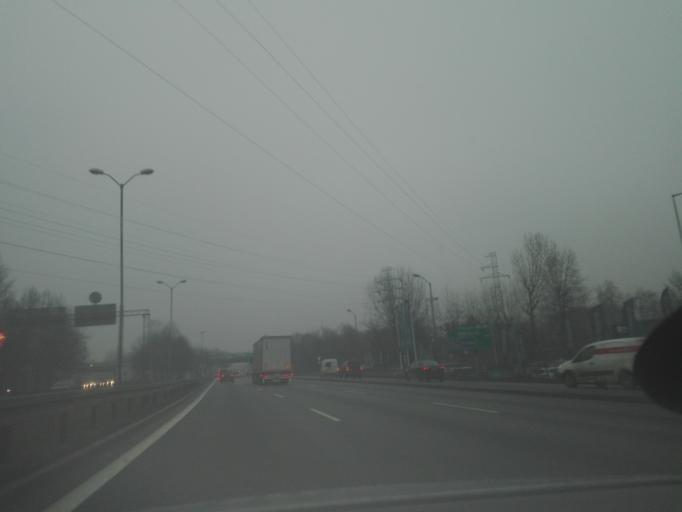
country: PL
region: Silesian Voivodeship
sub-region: Katowice
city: Katowice
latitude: 50.2620
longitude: 19.0433
